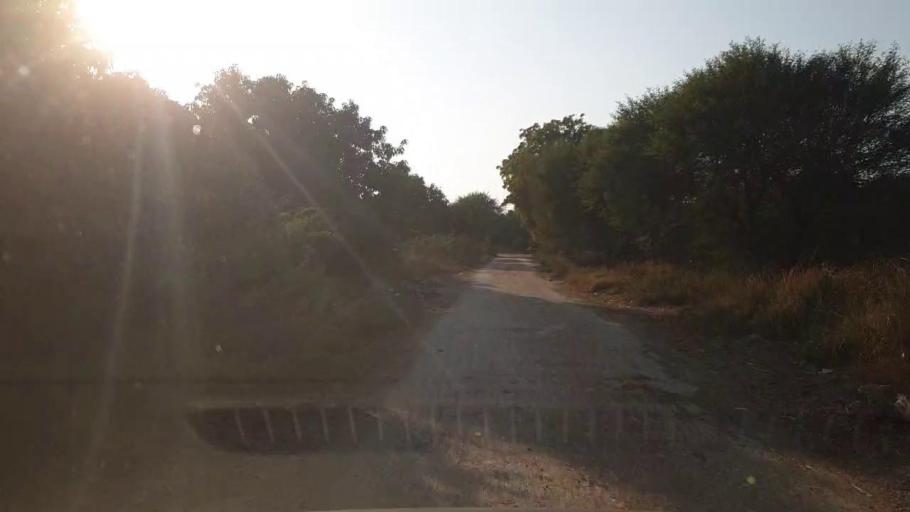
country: PK
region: Sindh
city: Chambar
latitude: 25.4160
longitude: 68.9009
